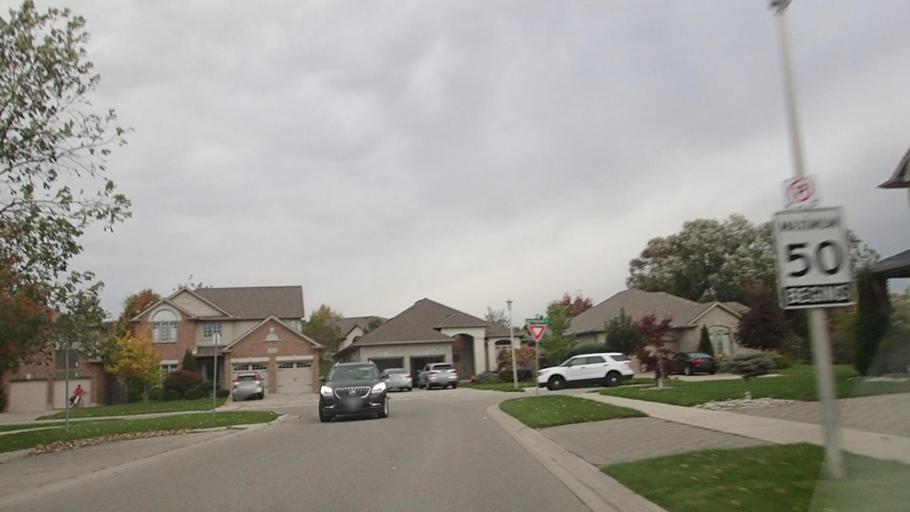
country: CA
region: Ontario
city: London
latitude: 43.0399
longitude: -81.2668
